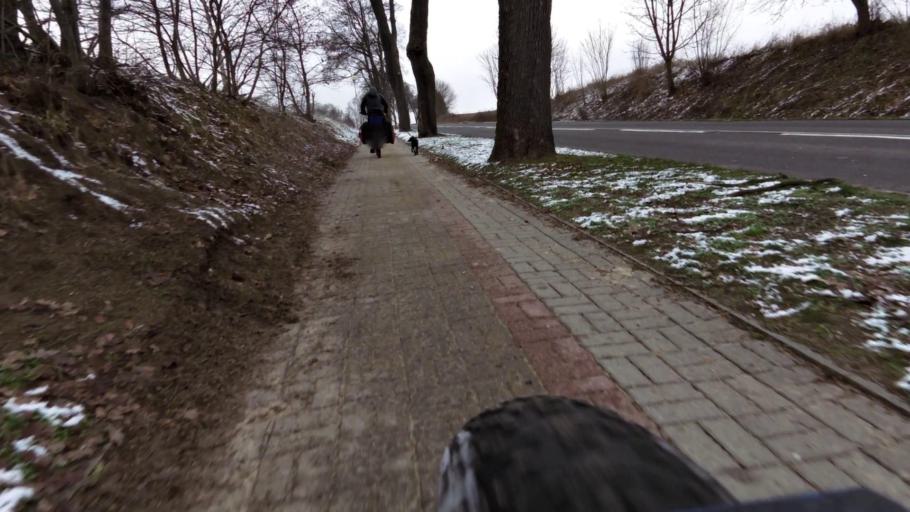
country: PL
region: West Pomeranian Voivodeship
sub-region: Powiat walecki
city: Miroslawiec
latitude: 53.3604
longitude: 16.0848
